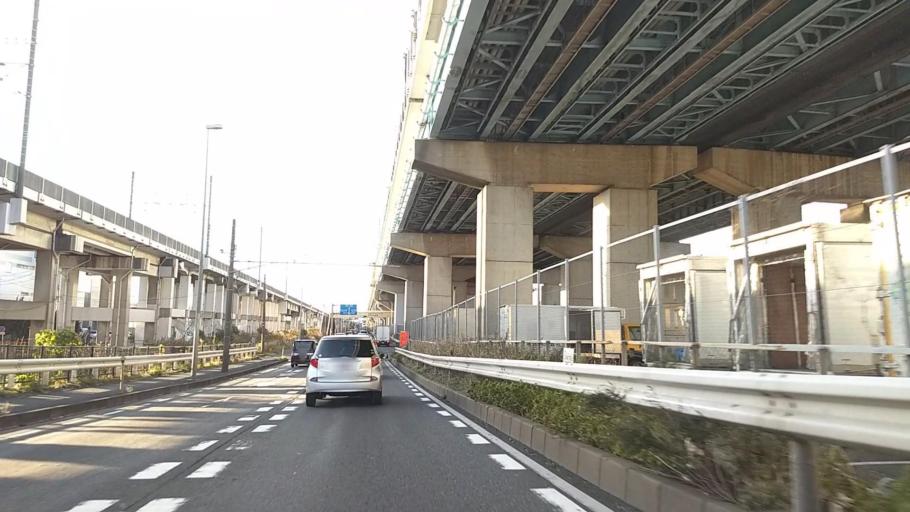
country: JP
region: Chiba
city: Funabashi
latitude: 35.6868
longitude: 139.9826
